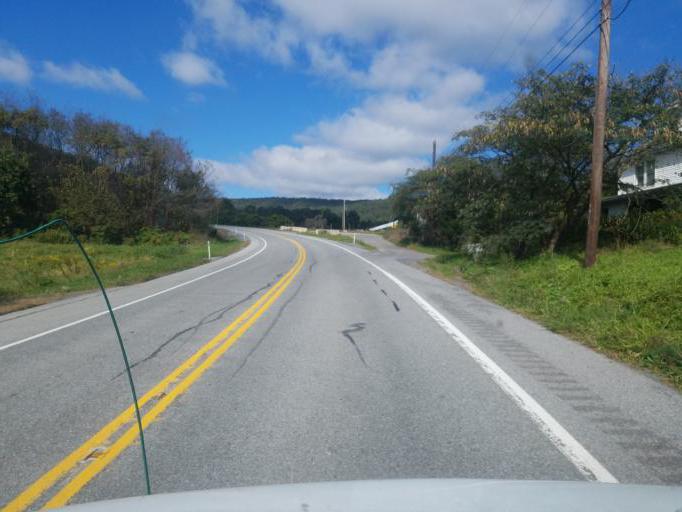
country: US
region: Pennsylvania
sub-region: Fulton County
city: McConnellsburg
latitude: 40.0115
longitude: -78.1111
